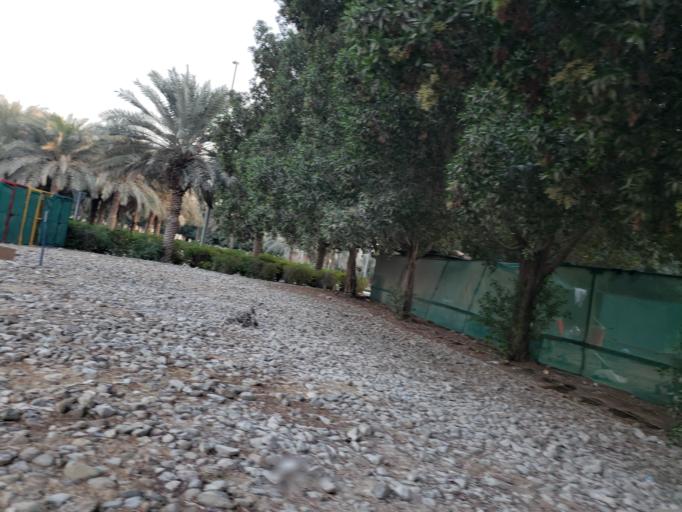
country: AE
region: Dubai
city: Dubai
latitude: 25.0091
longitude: 55.2506
